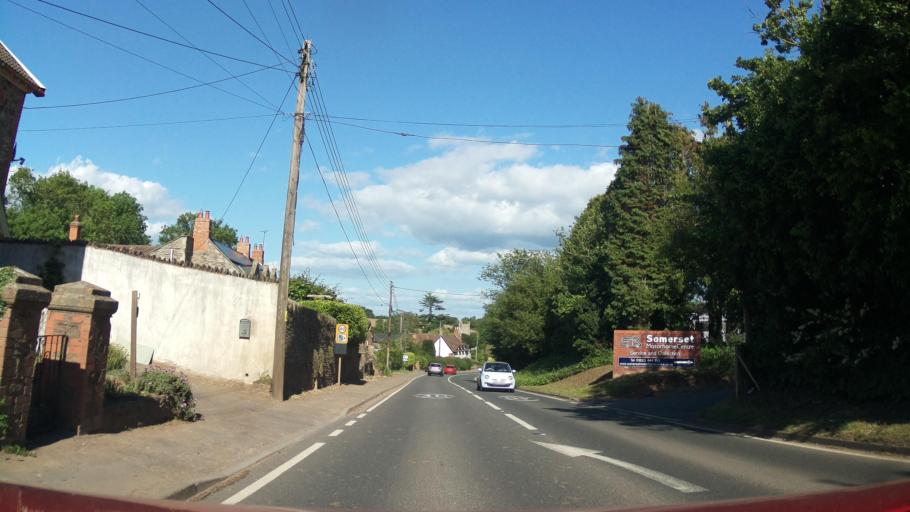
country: GB
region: England
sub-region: Somerset
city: Creech Saint Michael
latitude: 51.0479
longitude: -3.0185
